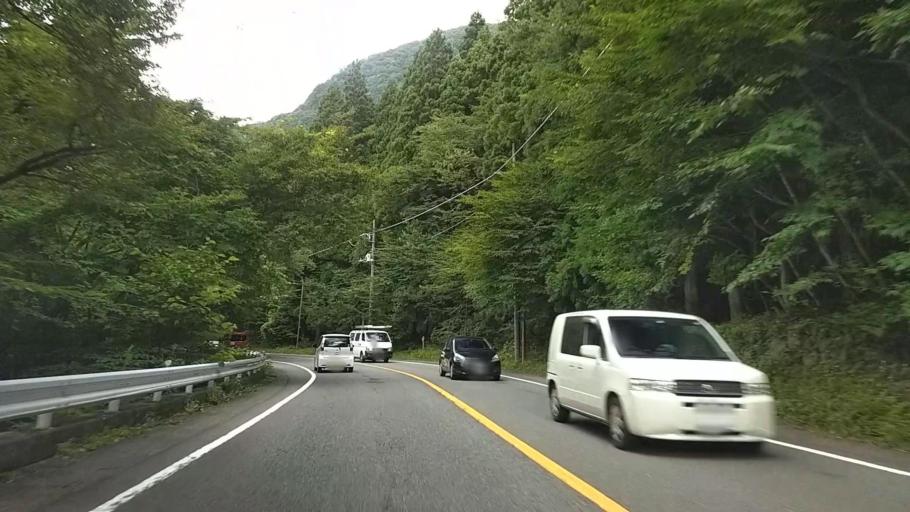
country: JP
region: Tochigi
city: Nikko
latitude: 36.7389
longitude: 139.5368
